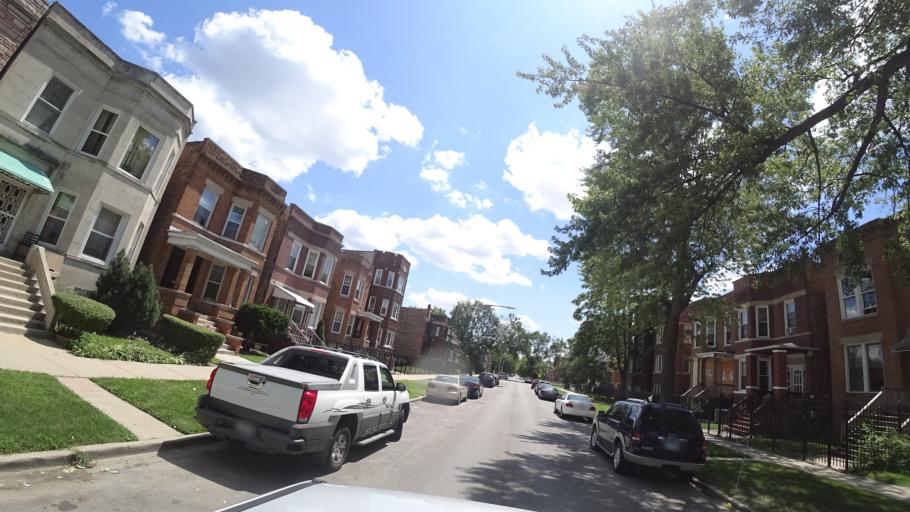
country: US
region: Illinois
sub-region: Cook County
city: Chicago
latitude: 41.7780
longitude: -87.6083
